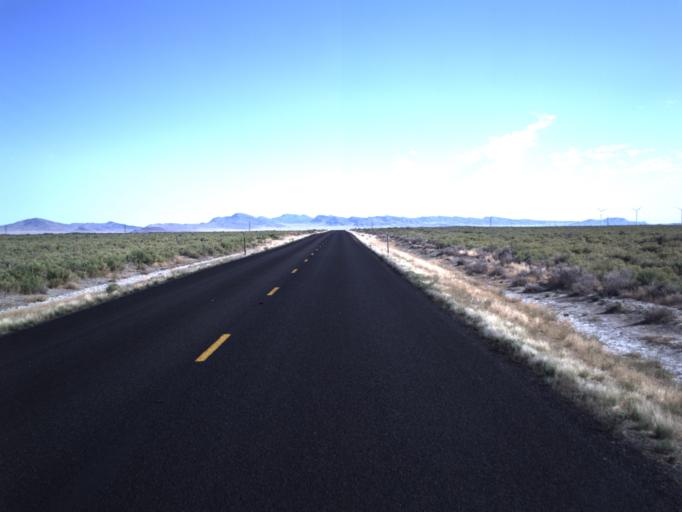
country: US
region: Utah
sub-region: Beaver County
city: Milford
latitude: 38.5491
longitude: -112.9912
